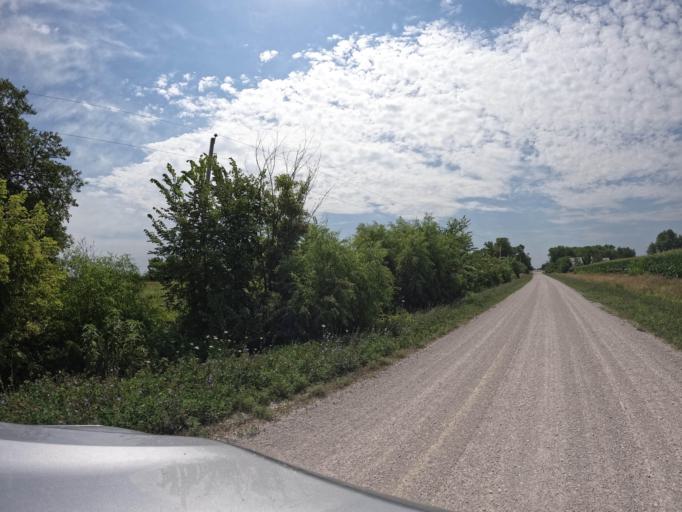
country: US
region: Iowa
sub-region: Appanoose County
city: Centerville
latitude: 40.8144
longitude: -92.9448
